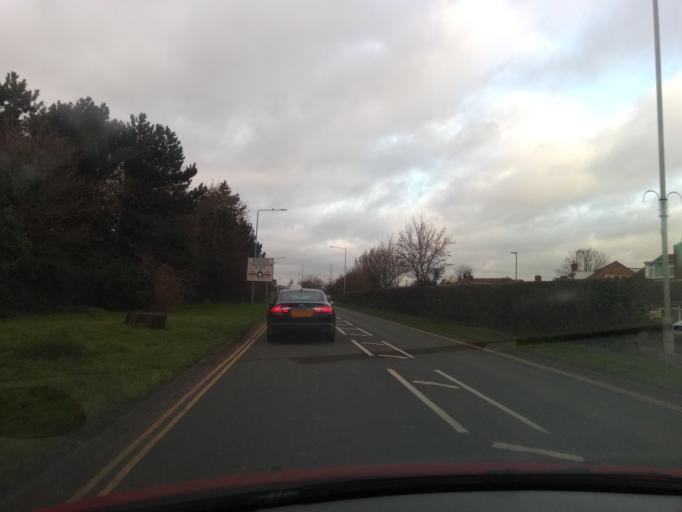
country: GB
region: England
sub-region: Leicestershire
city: Loughborough
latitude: 52.7608
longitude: -1.2101
